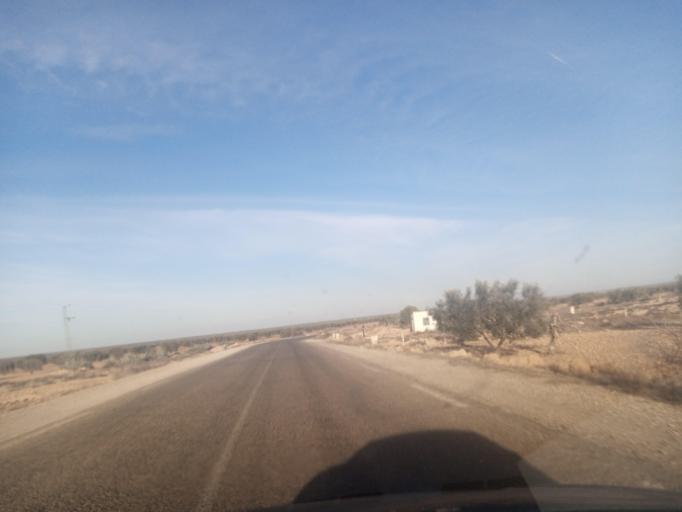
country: TN
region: Safaqis
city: Bi'r `Ali Bin Khalifah
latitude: 34.9294
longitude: 10.3236
